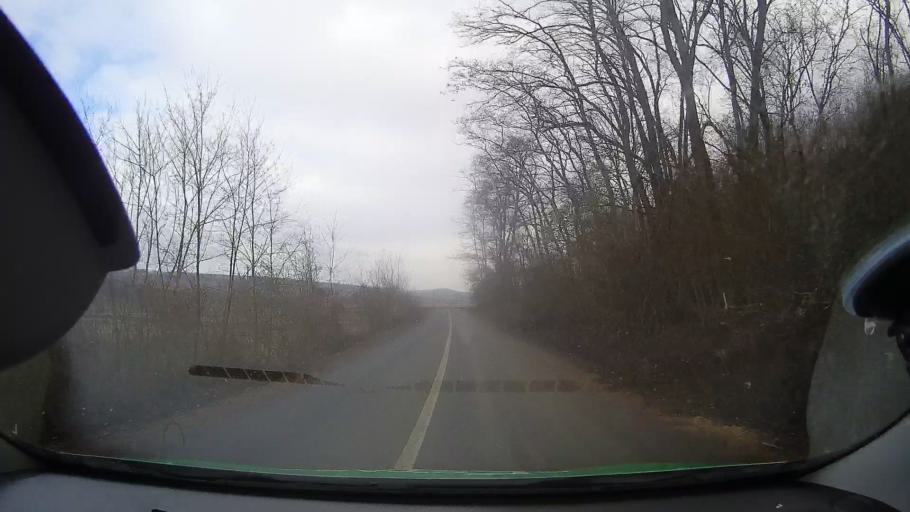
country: RO
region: Mures
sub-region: Comuna Ludus
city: Gheja
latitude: 46.4062
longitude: 24.0657
